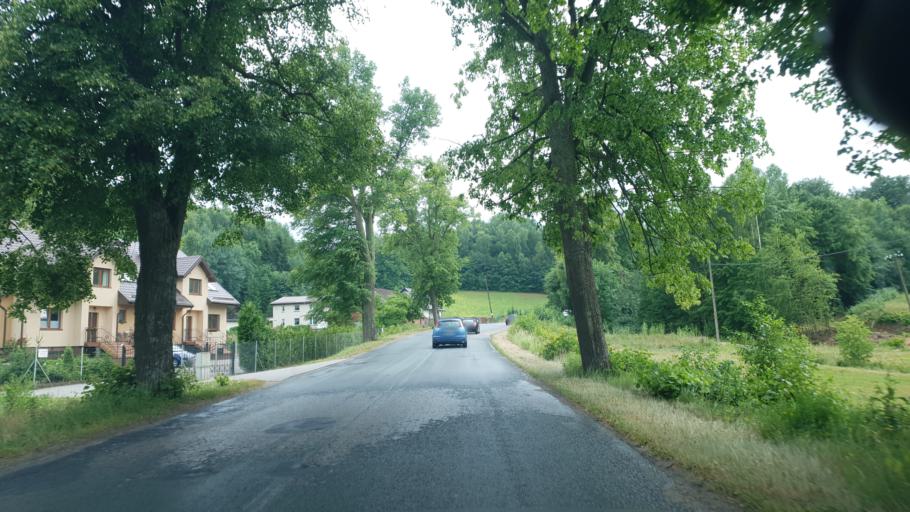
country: PL
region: Pomeranian Voivodeship
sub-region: Powiat kartuski
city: Chmielno
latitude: 54.2798
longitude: 18.1002
